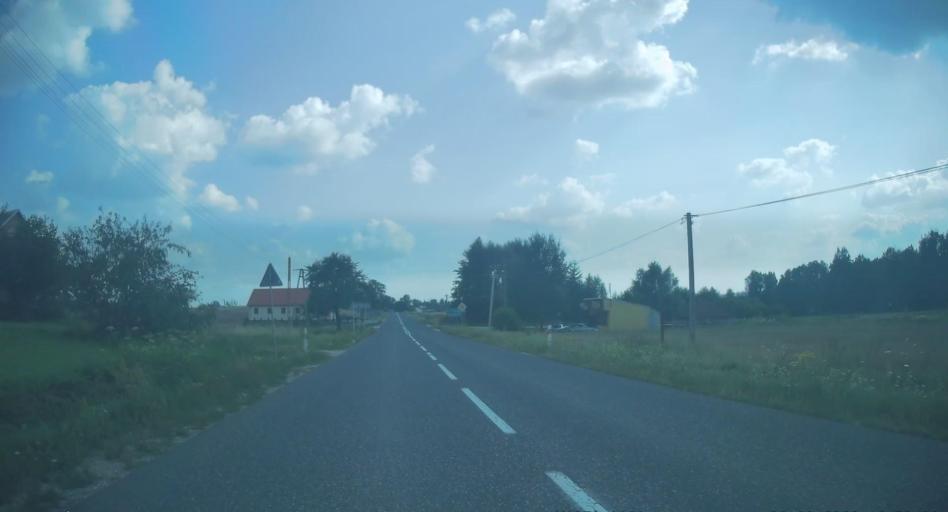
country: PL
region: Swietokrzyskie
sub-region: Powiat kielecki
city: Lopuszno
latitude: 50.9145
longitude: 20.2438
